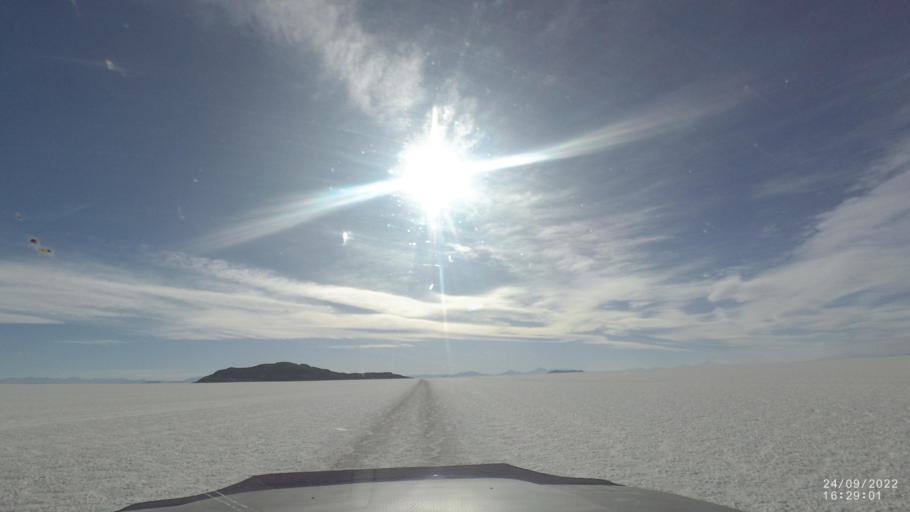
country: BO
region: Potosi
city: Colchani
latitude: -20.2406
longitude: -67.6088
